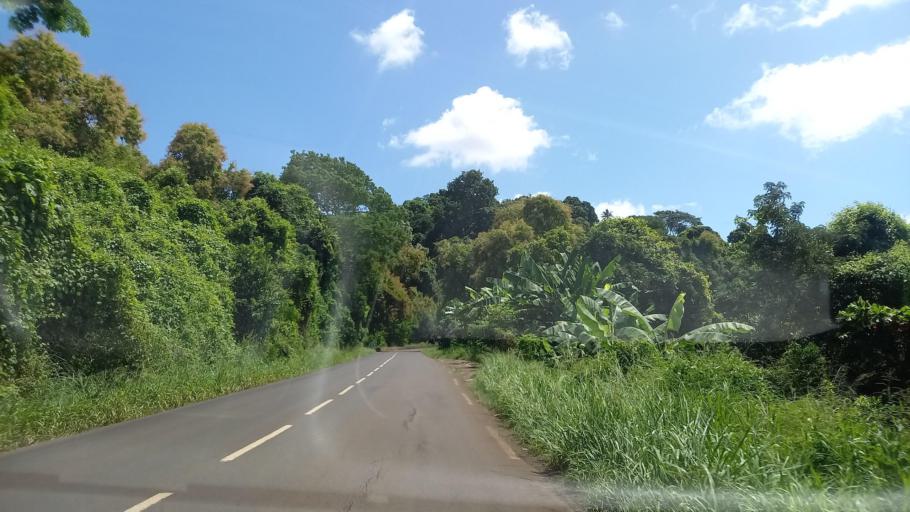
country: YT
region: Bandraboua
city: Bandraboua
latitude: -12.7203
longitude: 45.1294
